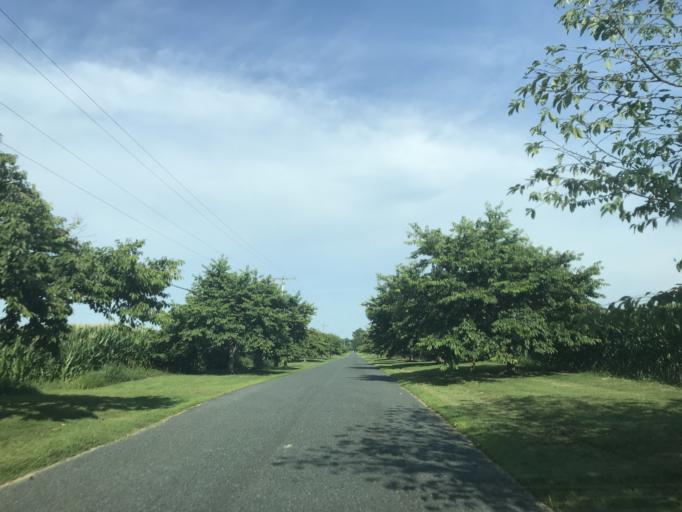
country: US
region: Maryland
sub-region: Harford County
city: Havre de Grace
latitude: 39.5220
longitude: -76.1190
